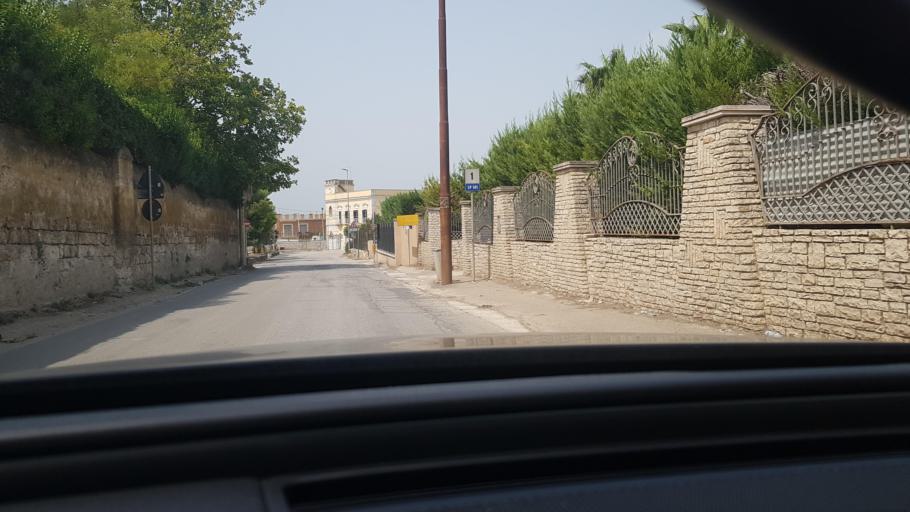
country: IT
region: Apulia
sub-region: Provincia di Barletta - Andria - Trani
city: Andria
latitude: 41.2328
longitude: 16.2691
